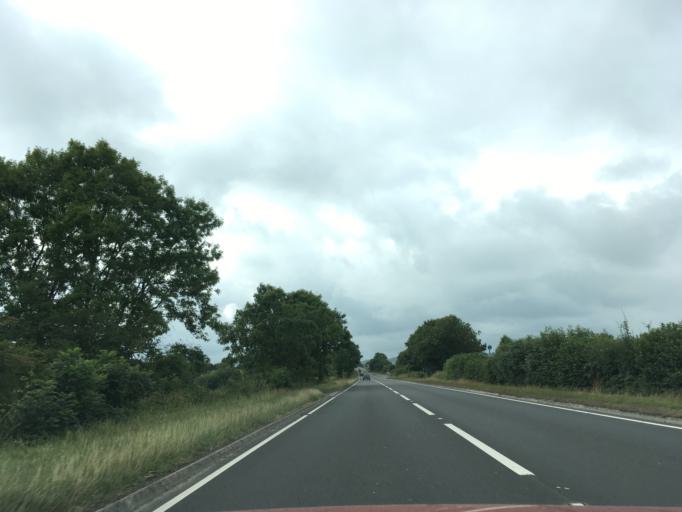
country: GB
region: Wales
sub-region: Carmarthenshire
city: Llanddowror
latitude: 51.8224
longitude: -4.5278
